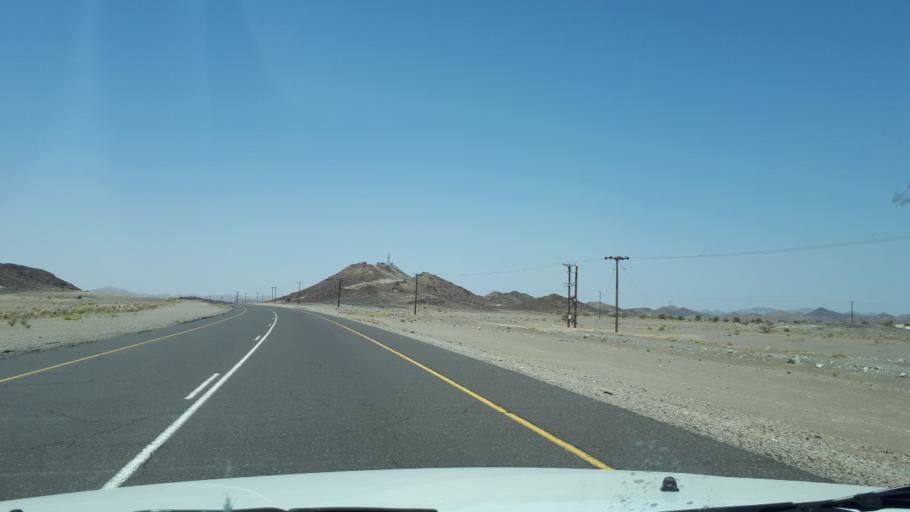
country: OM
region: Ash Sharqiyah
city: Ibra'
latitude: 22.6316
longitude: 58.4613
